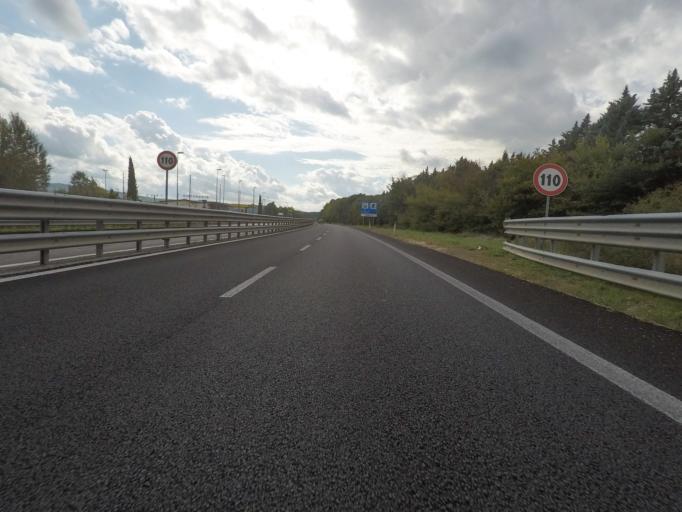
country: IT
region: Tuscany
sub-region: Provincia di Siena
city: Serre di Rapolano
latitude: 43.2648
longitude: 11.6293
